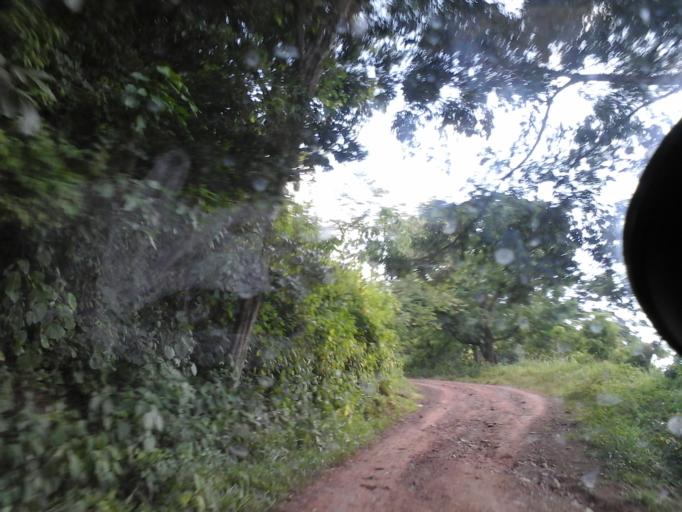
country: CO
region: Cesar
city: San Diego
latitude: 10.2515
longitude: -73.1124
